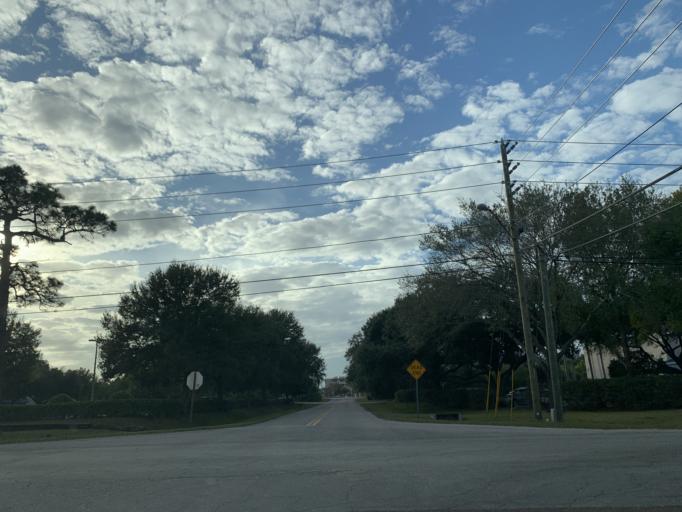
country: US
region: Florida
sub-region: Pinellas County
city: South Highpoint
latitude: 27.9029
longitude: -82.6963
